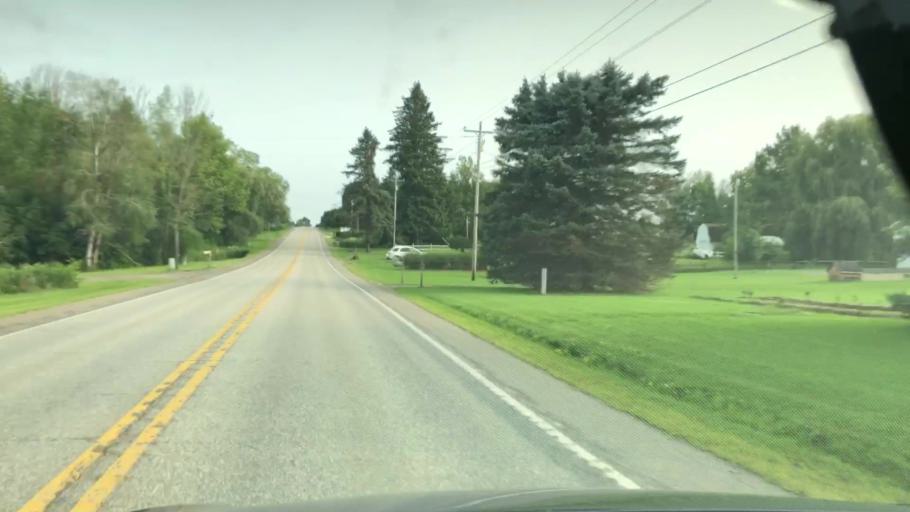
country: US
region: Pennsylvania
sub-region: Erie County
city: Union City
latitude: 41.8787
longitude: -79.8425
